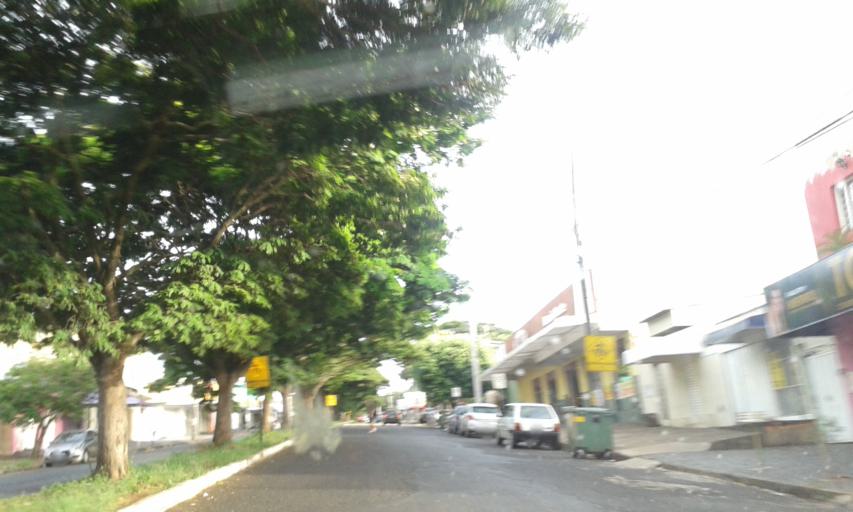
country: BR
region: Minas Gerais
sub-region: Uberlandia
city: Uberlandia
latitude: -18.9075
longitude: -48.2462
